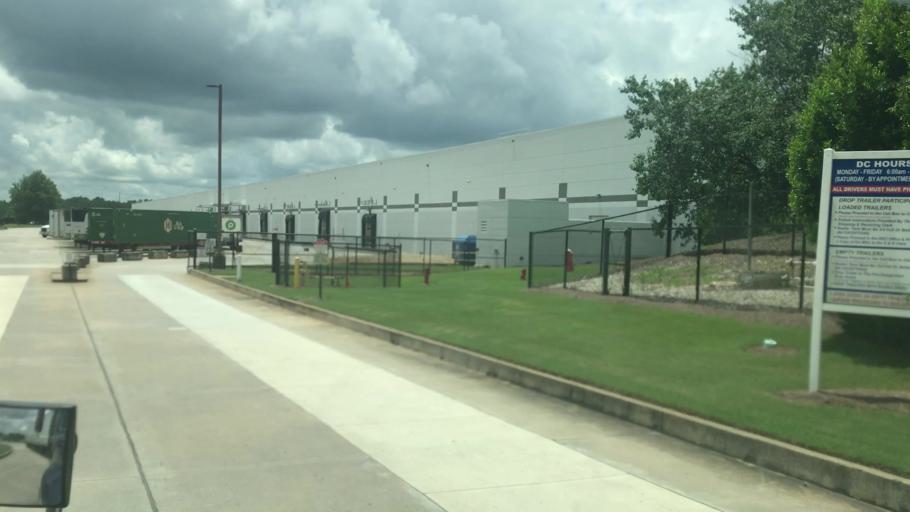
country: US
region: Georgia
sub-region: Henry County
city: McDonough
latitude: 33.4113
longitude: -84.1555
